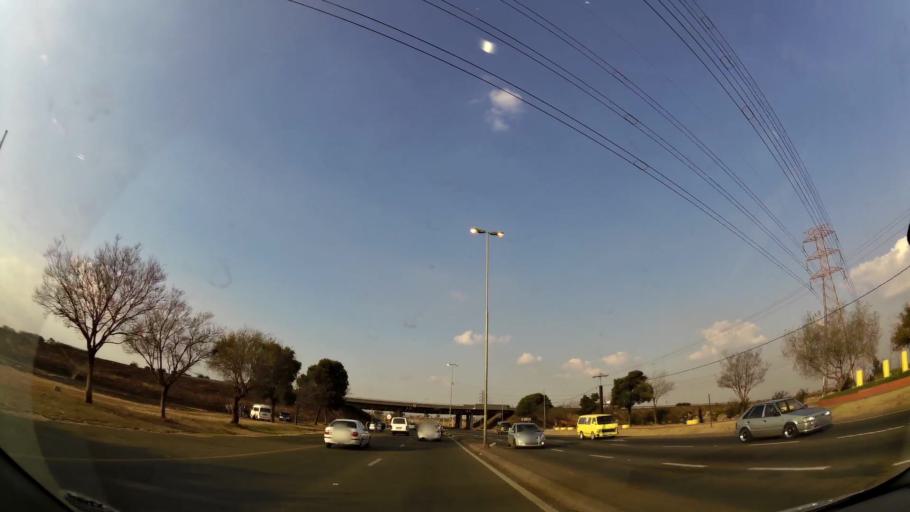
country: ZA
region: Gauteng
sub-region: Ekurhuleni Metropolitan Municipality
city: Germiston
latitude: -26.3417
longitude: 28.2189
